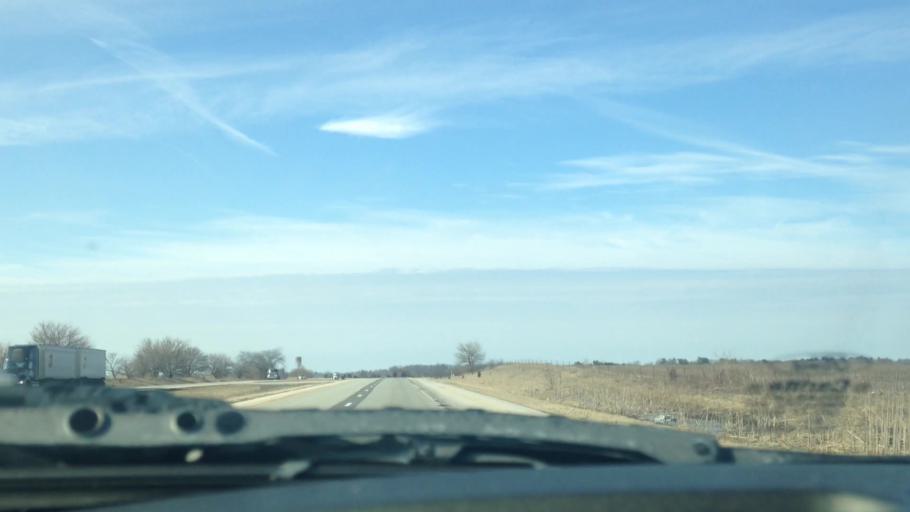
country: US
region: Illinois
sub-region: Ford County
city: Paxton
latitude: 40.5324
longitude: -88.0768
